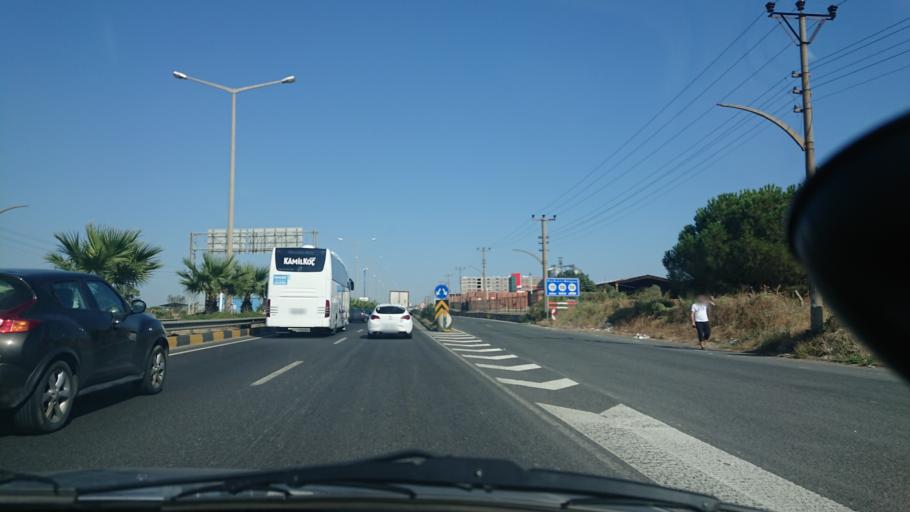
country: TR
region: Manisa
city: Turgutlu
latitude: 38.4920
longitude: 27.6651
